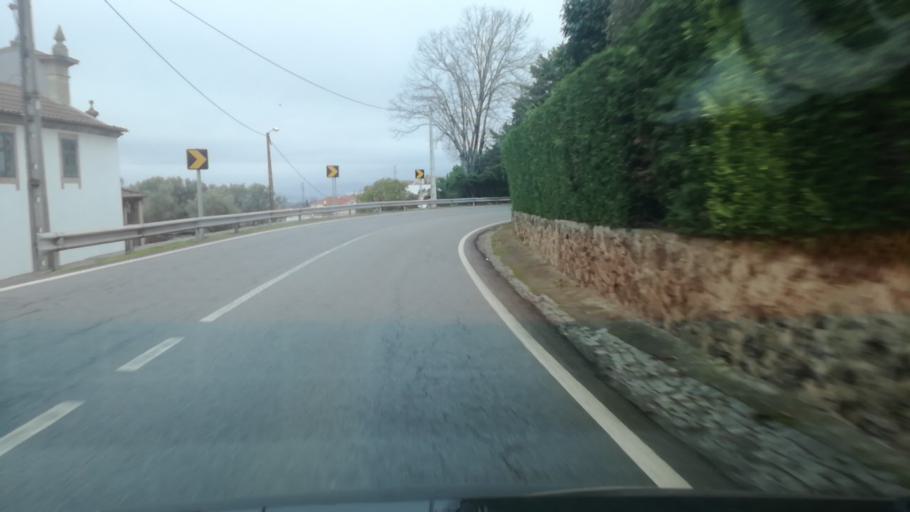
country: PT
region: Braga
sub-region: Braga
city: Braga
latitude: 41.5315
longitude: -8.4003
